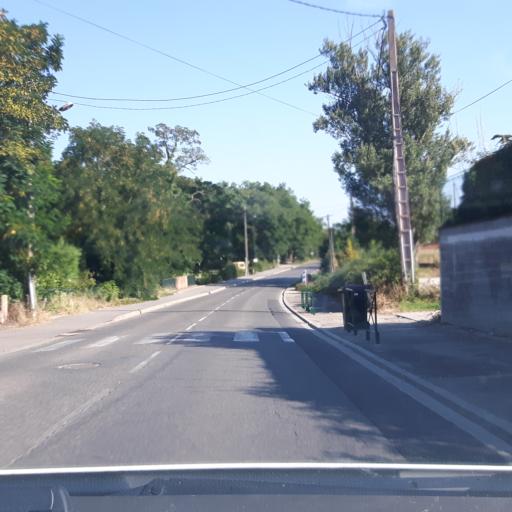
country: FR
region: Midi-Pyrenees
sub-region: Departement de la Haute-Garonne
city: Fronton
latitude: 43.8384
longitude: 1.3934
